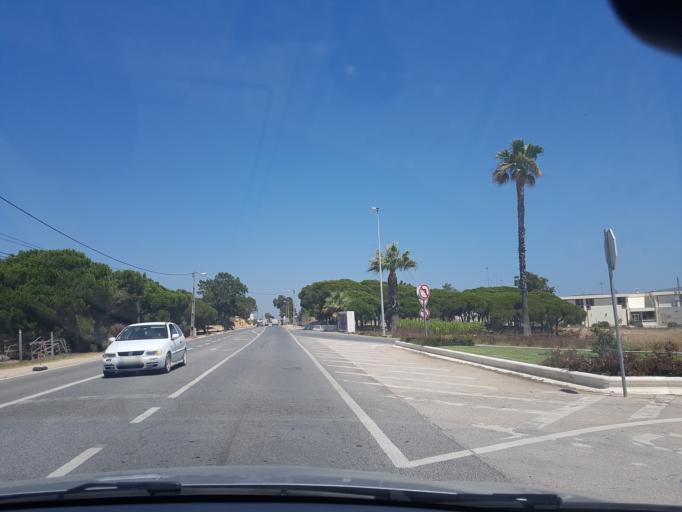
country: PT
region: Faro
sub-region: Faro
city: Faro
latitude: 37.0224
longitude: -7.9750
